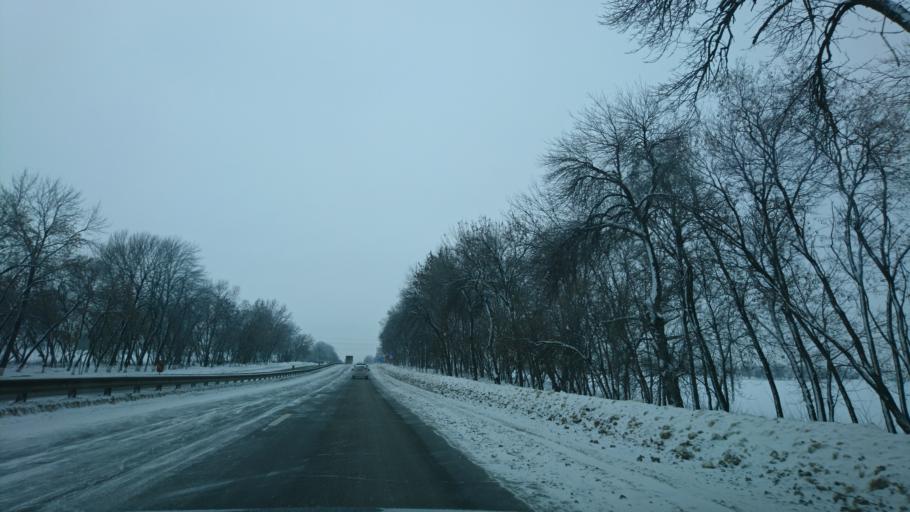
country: RU
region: Belgorod
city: Mayskiy
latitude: 50.4397
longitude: 36.3930
